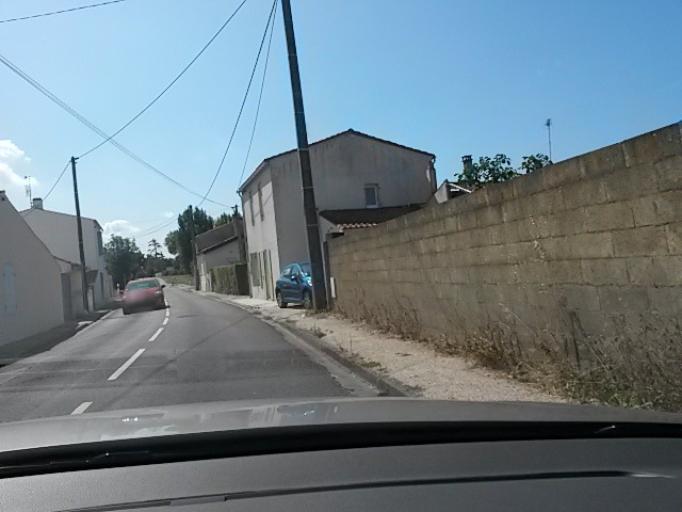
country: FR
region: Poitou-Charentes
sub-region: Departement de la Charente-Maritime
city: Marennes
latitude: 45.8323
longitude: -1.0968
